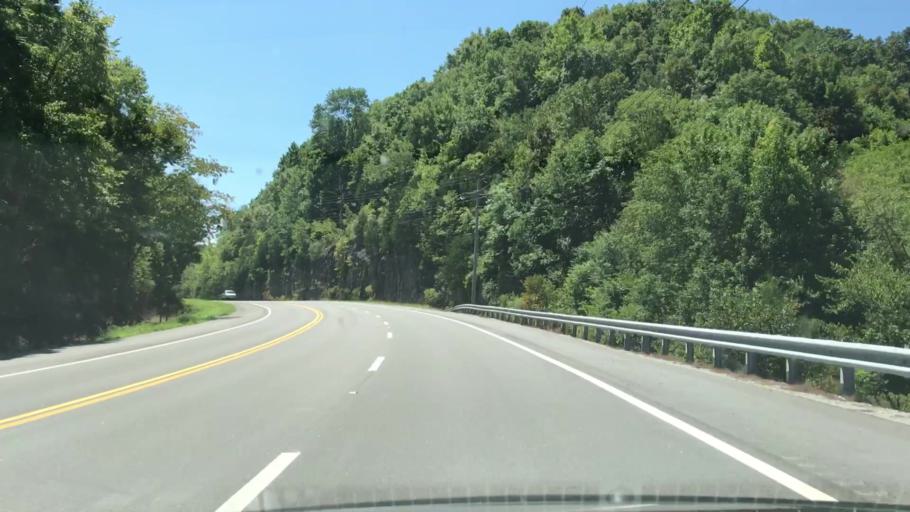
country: US
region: Tennessee
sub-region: Clay County
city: Celina
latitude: 36.5376
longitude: -85.5074
